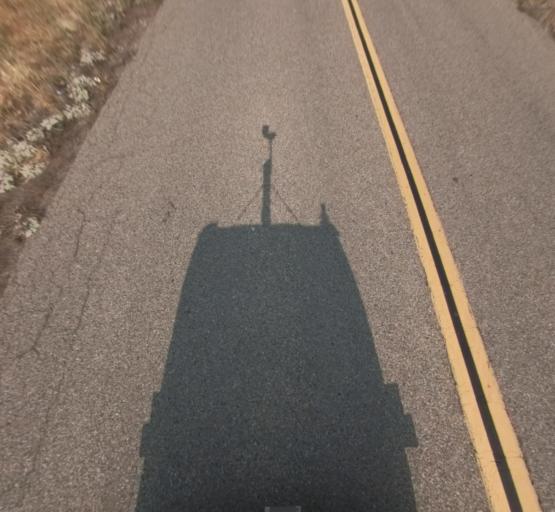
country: US
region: California
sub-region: Madera County
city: Madera Acres
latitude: 37.1193
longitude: -119.9664
